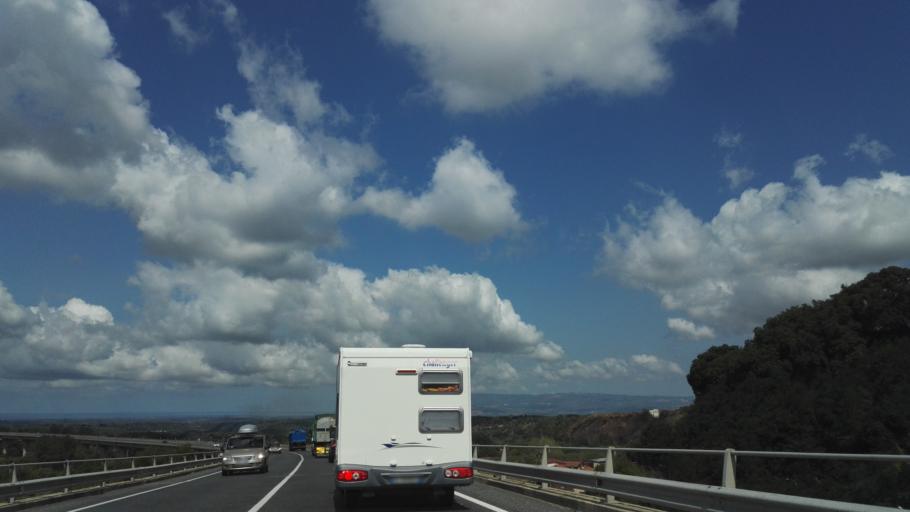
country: IT
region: Calabria
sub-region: Provincia di Reggio Calabria
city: Anoia Superiore
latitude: 38.4195
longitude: 16.1014
